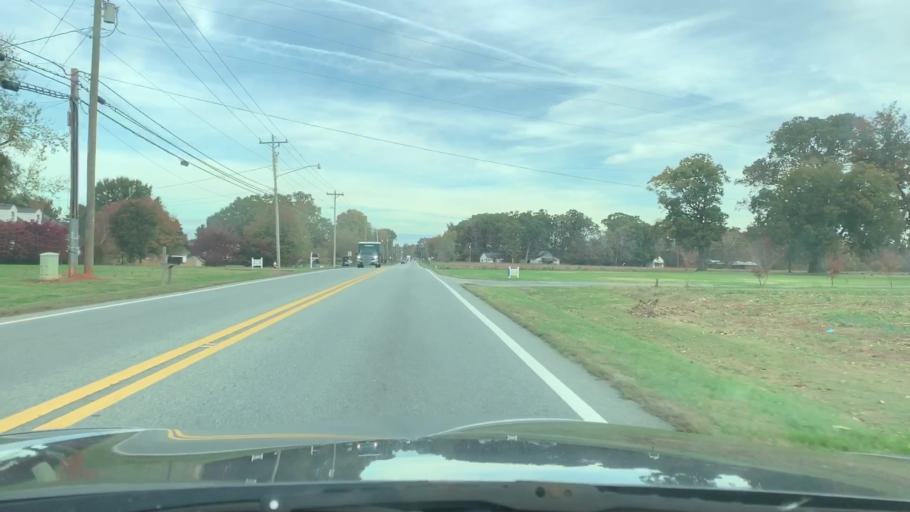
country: US
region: North Carolina
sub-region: Alamance County
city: Green Level
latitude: 36.1065
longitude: -79.3529
